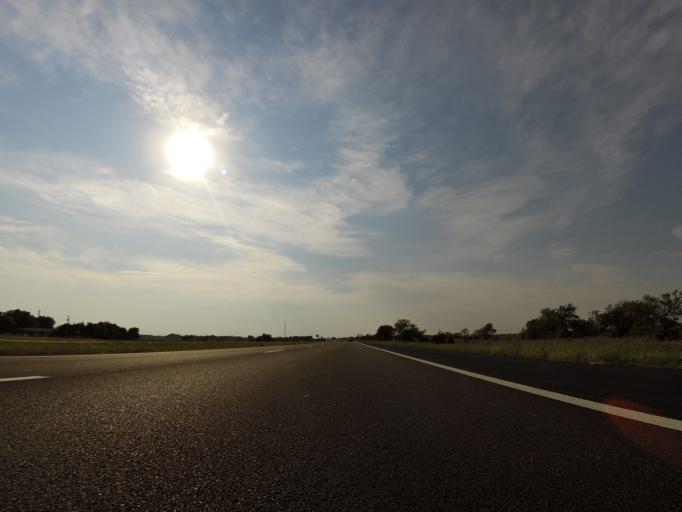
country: US
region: Kansas
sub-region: Reno County
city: Haven
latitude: 37.8911
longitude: -97.7544
